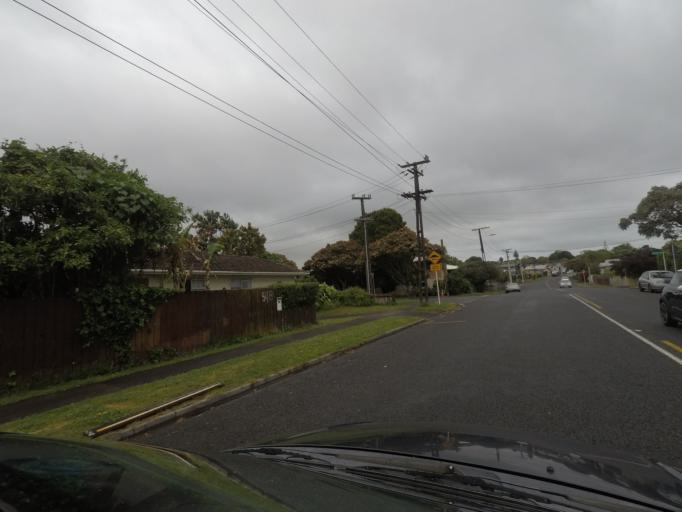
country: NZ
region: Auckland
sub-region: Auckland
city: Auckland
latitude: -36.8892
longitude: 174.7322
